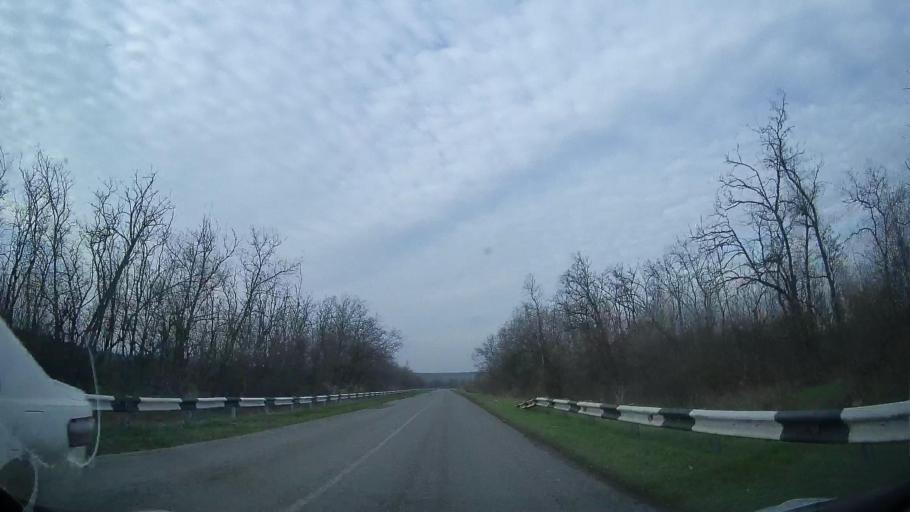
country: RU
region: Rostov
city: Zernograd
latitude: 46.8860
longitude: 40.3415
